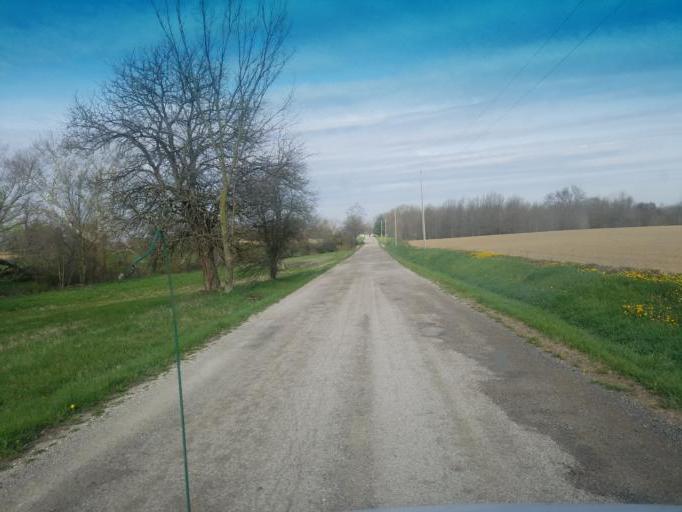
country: US
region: Ohio
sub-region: Delaware County
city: Ashley
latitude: 40.4393
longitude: -82.9653
